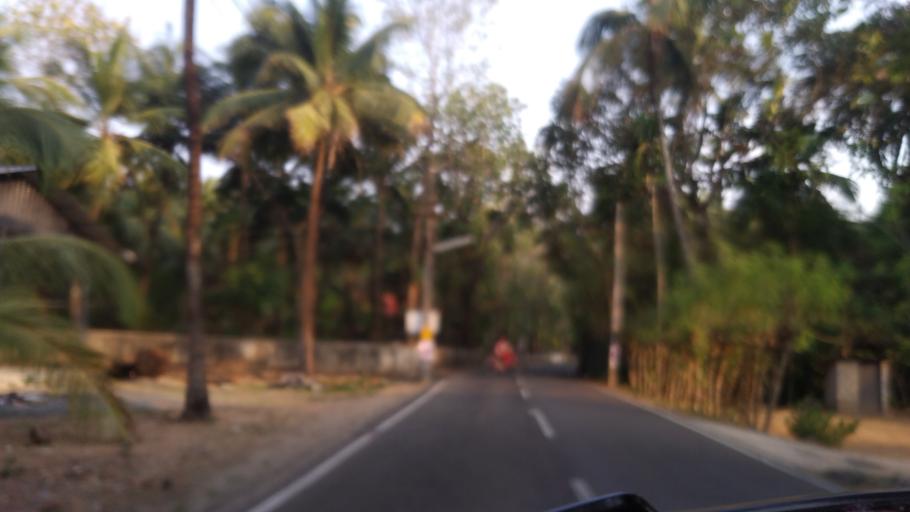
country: IN
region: Kerala
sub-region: Thrissur District
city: Thanniyam
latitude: 10.4050
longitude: 76.0954
